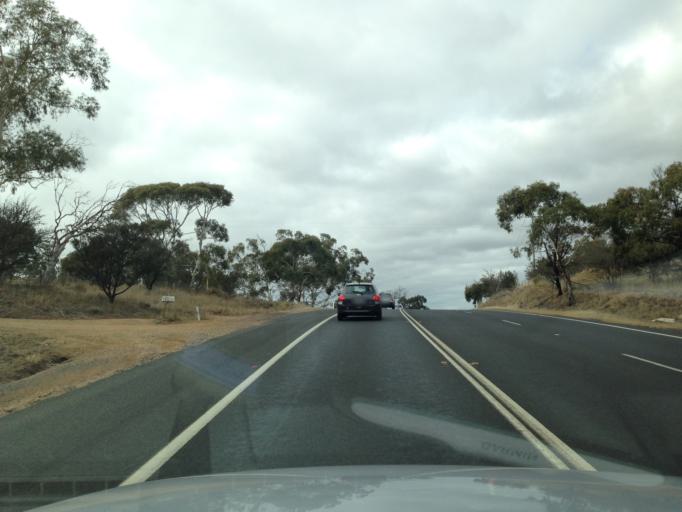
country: AU
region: New South Wales
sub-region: Cooma-Monaro
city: Cooma
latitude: -36.2404
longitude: 149.0735
